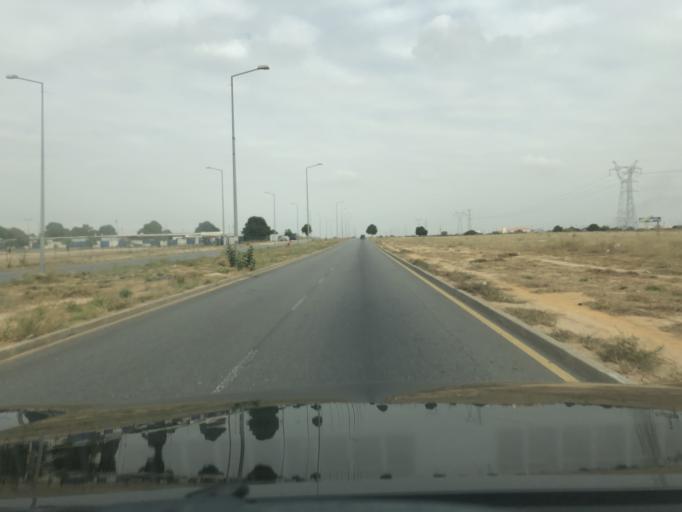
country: AO
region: Luanda
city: Luanda
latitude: -8.9757
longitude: 13.2838
